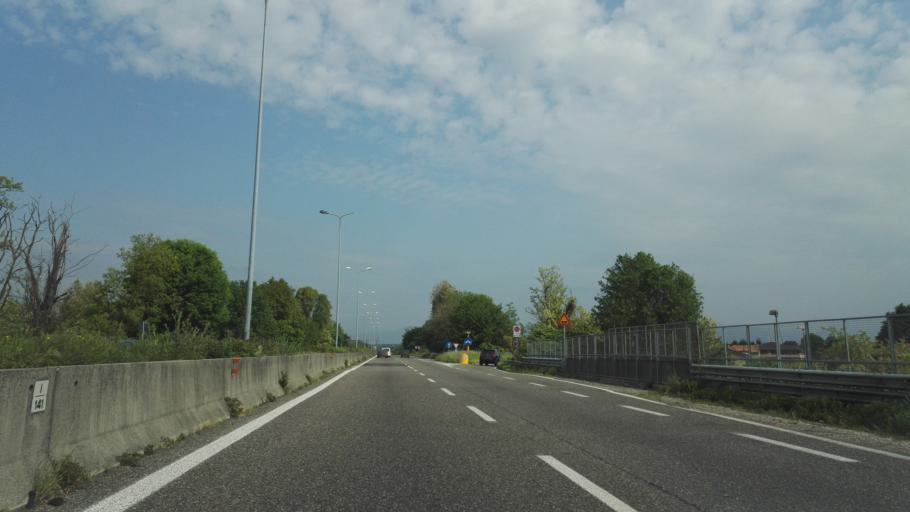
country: IT
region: Lombardy
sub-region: Provincia di Monza e Brianza
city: Cesano Maderno
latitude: 45.6370
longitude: 9.1596
